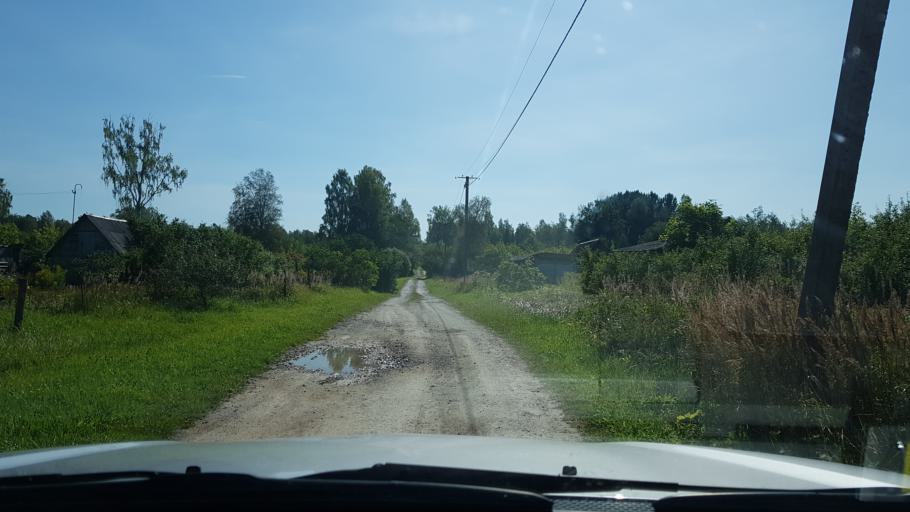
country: EE
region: Ida-Virumaa
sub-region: Sillamaee linn
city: Sillamae
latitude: 59.3195
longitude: 27.7820
